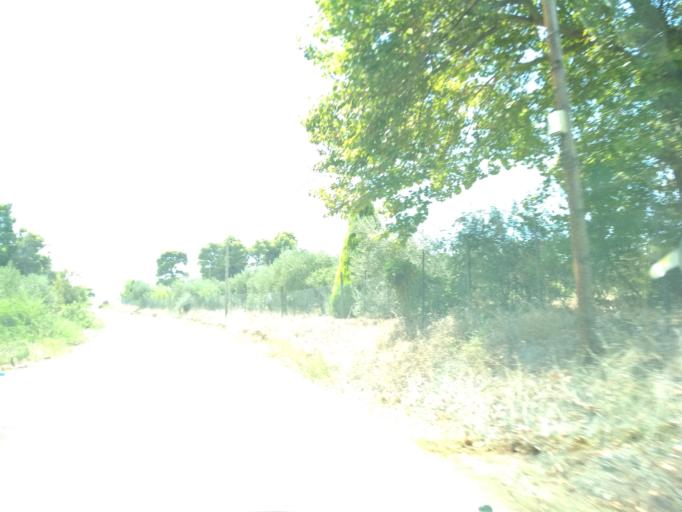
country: GR
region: Central Greece
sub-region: Nomos Evvoias
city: Roviai
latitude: 38.8241
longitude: 23.2430
